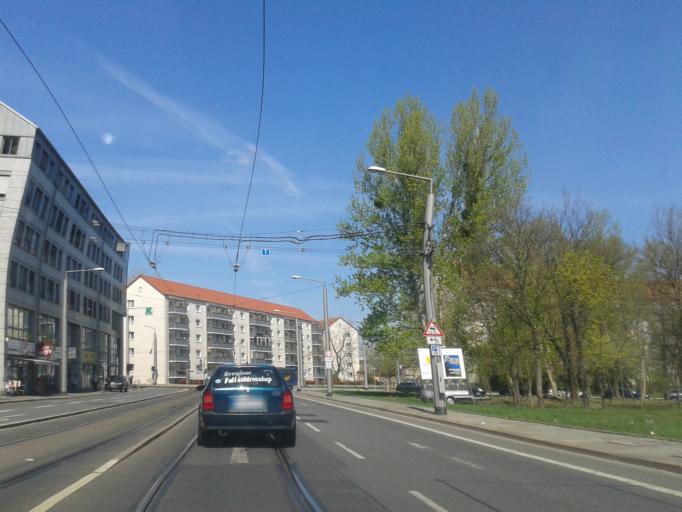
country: DE
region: Saxony
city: Dresden
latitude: 51.0511
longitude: 13.7291
